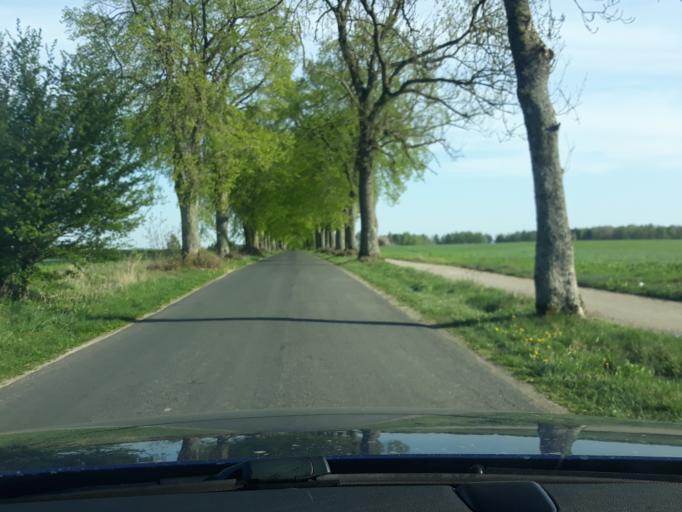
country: PL
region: Pomeranian Voivodeship
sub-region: Powiat czluchowski
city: Przechlewo
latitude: 53.8390
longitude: 17.3637
